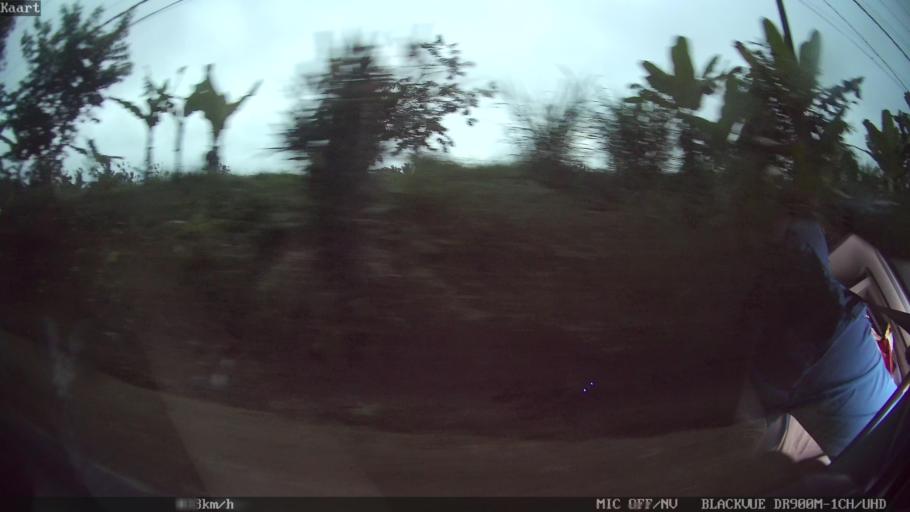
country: ID
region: Bali
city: Banjar Buahan
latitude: -8.4060
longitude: 115.2462
